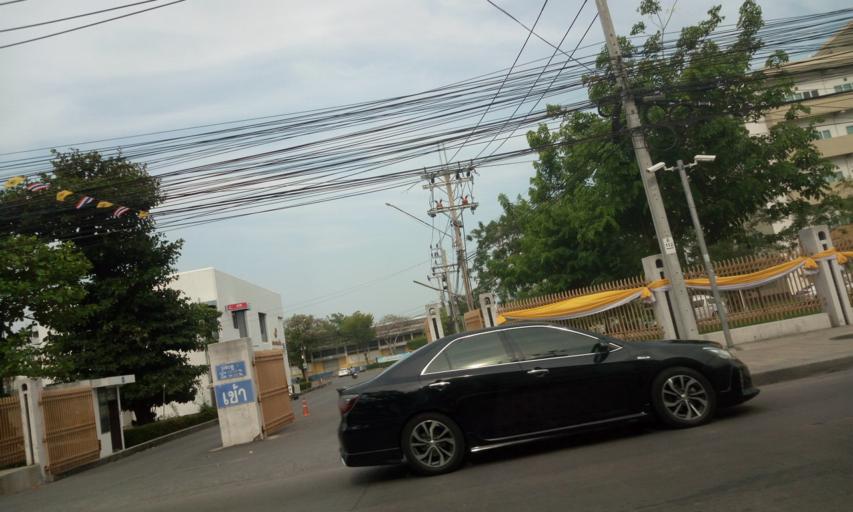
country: TH
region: Bangkok
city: Bang Na
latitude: 13.6685
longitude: 100.6838
